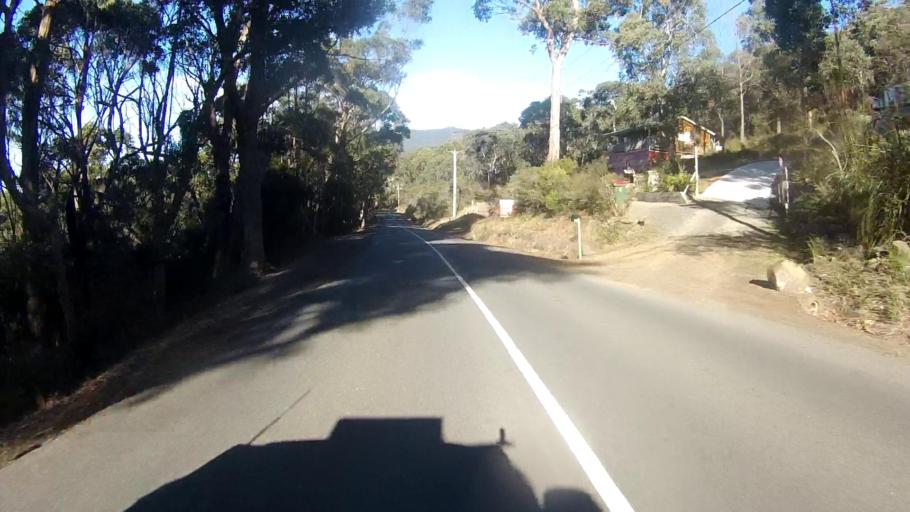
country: AU
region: Tasmania
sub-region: Clarence
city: Sandford
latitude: -43.0295
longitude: 147.9272
